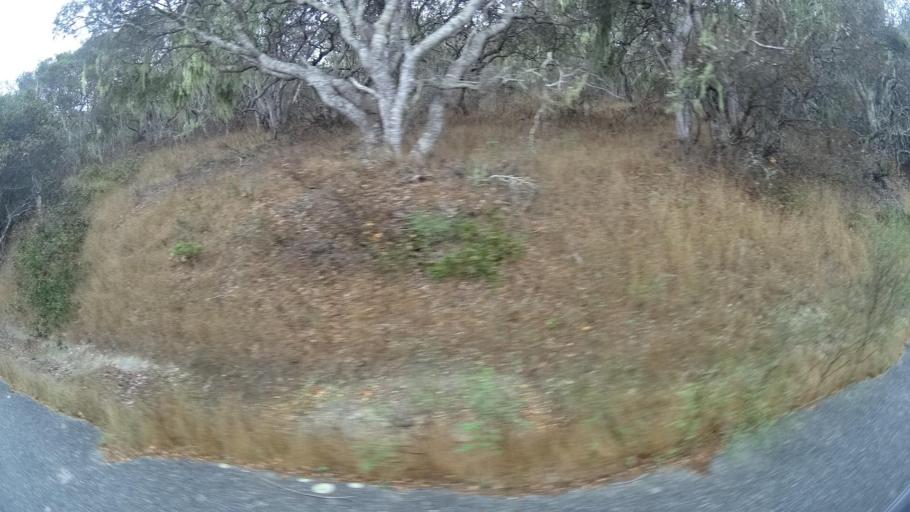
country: US
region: California
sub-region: Monterey County
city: Marina
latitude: 36.6512
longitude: -121.7500
